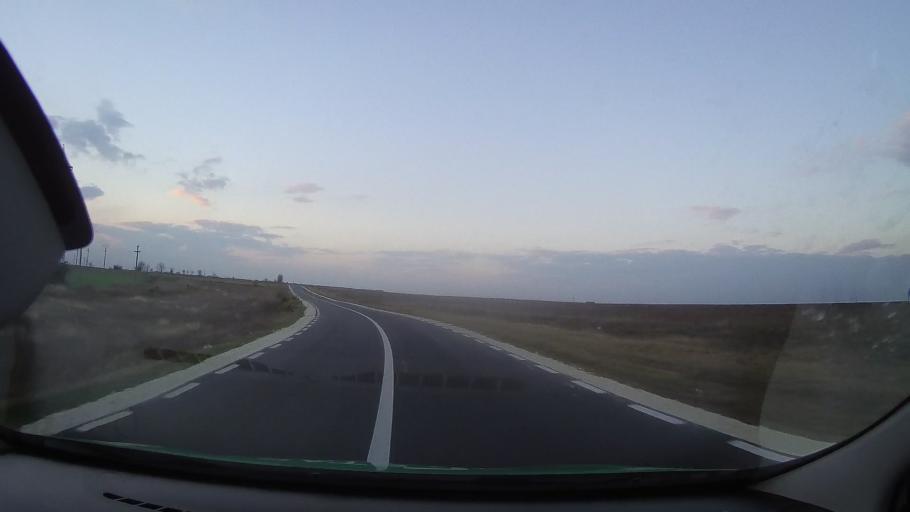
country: RO
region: Constanta
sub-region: Comuna Baneasa
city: Baneasa
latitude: 44.0936
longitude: 27.6866
